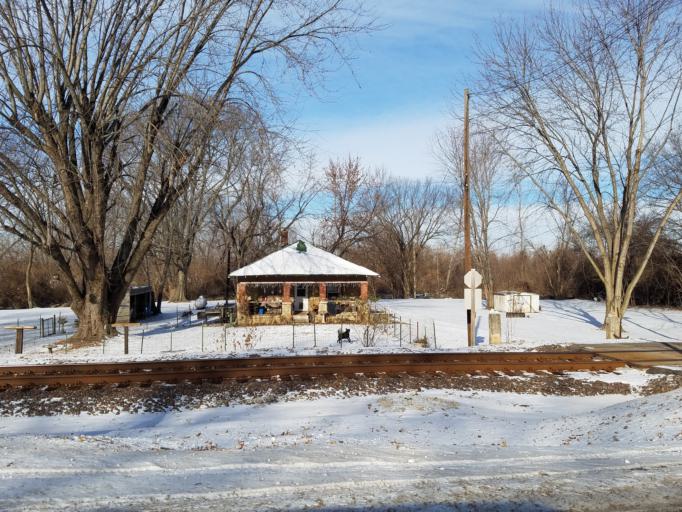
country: US
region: Missouri
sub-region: Lafayette County
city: Lexington
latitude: 39.1501
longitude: -93.9473
